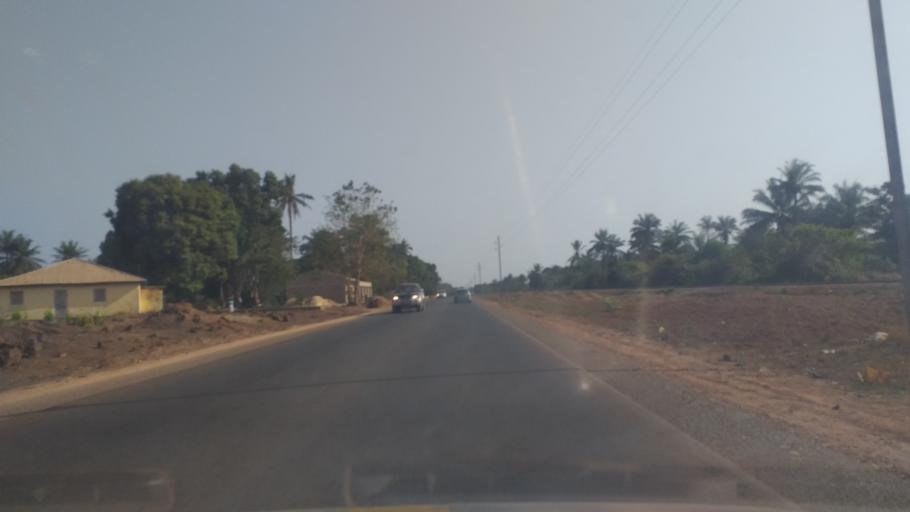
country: GN
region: Boke
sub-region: Boke Prefecture
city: Kamsar
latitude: 10.7233
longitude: -14.5197
